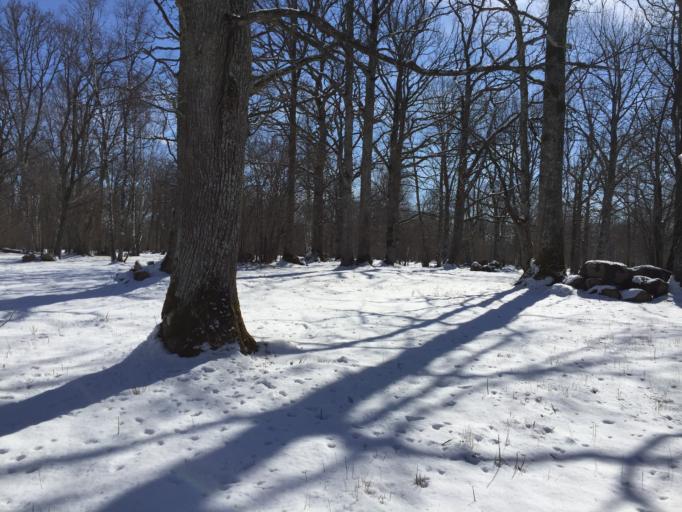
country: EE
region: Laeaene
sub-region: Lihula vald
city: Lihula
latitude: 58.5379
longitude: 24.0735
